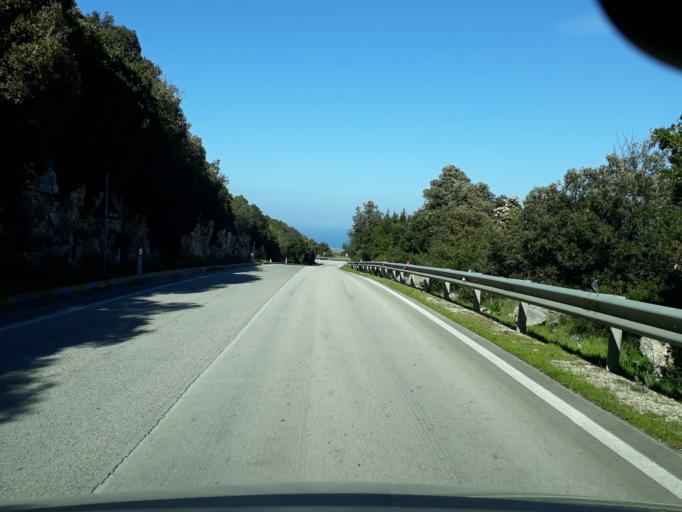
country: IT
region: Apulia
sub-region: Provincia di Bari
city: Cozzana
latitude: 40.8806
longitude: 17.2750
